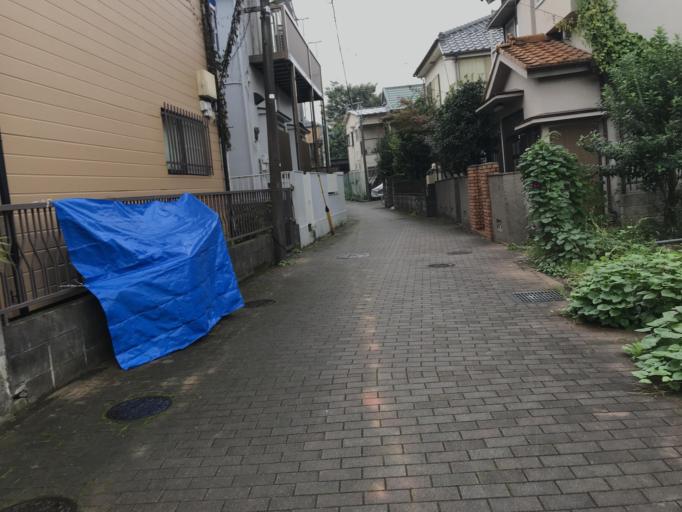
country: JP
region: Saitama
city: Wako
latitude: 35.7413
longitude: 139.6404
